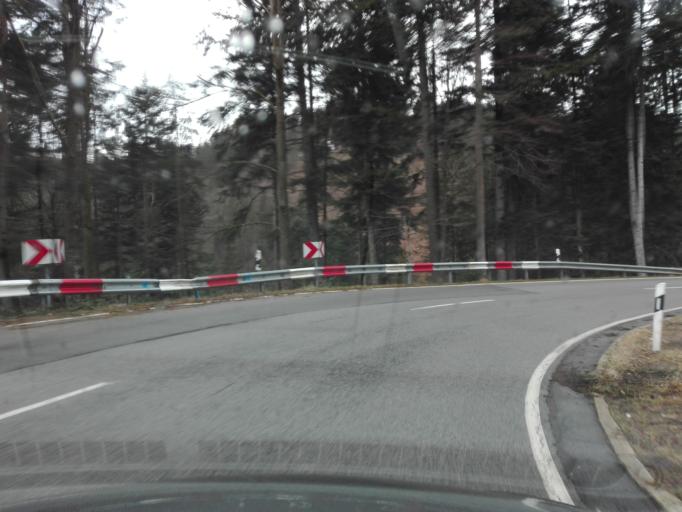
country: DE
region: Bavaria
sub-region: Lower Bavaria
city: Thyrnau
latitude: 48.5906
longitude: 13.5834
